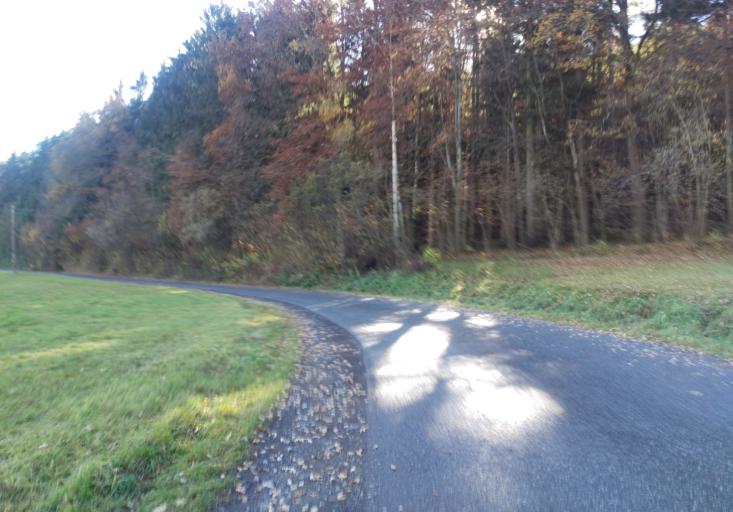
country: AT
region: Styria
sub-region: Graz Stadt
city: Mariatrost
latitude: 47.1302
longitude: 15.4843
